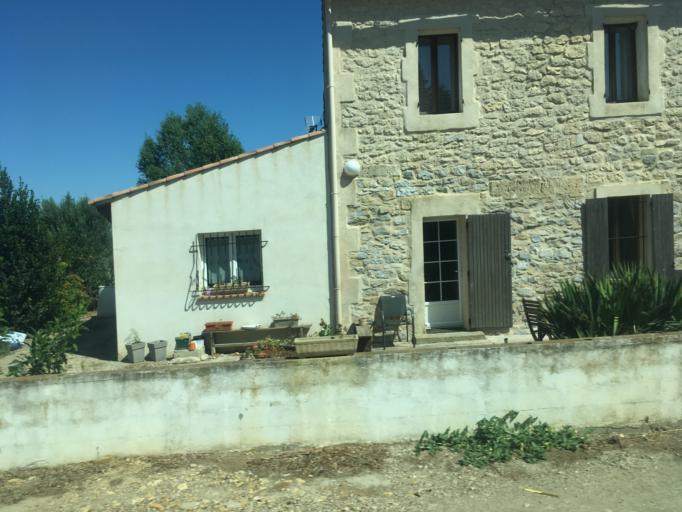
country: FR
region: Languedoc-Roussillon
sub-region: Departement du Gard
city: Saint-Gilles
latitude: 43.5784
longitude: 4.4538
